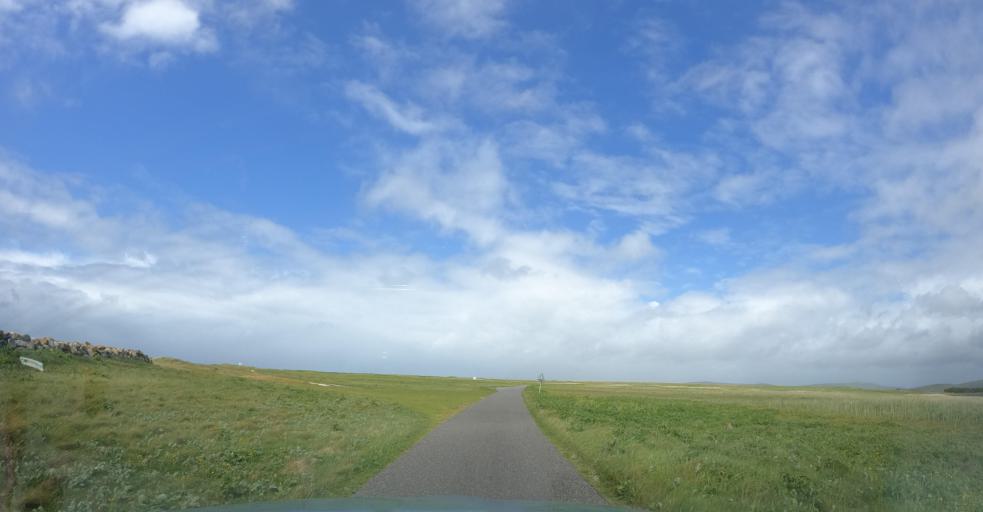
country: GB
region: Scotland
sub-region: Eilean Siar
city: Isle of South Uist
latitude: 57.2834
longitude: -7.4196
